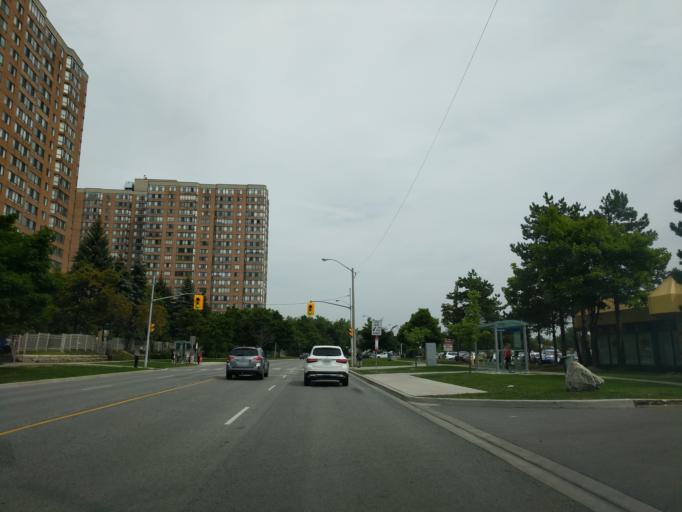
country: CA
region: Ontario
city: Markham
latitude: 43.8140
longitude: -79.3244
